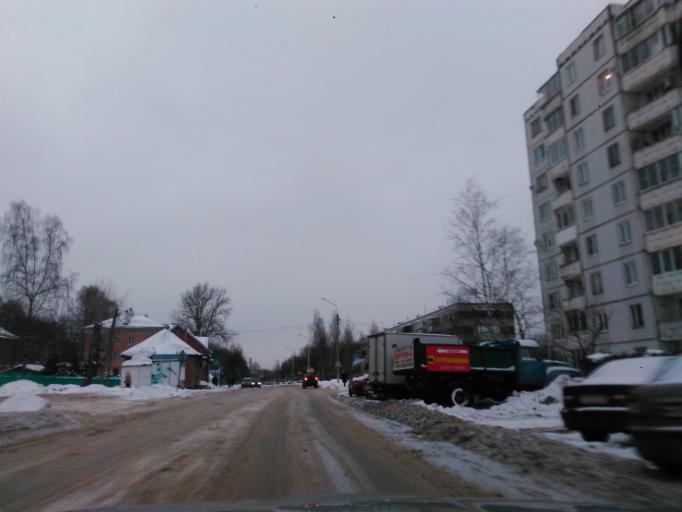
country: RU
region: Moskovskaya
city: Yakhroma
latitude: 56.2840
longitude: 37.4890
